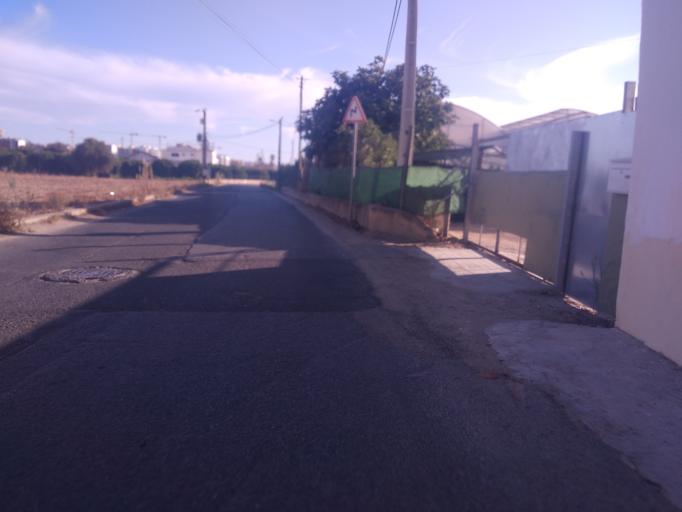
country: PT
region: Faro
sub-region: Faro
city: Faro
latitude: 37.0390
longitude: -7.9398
